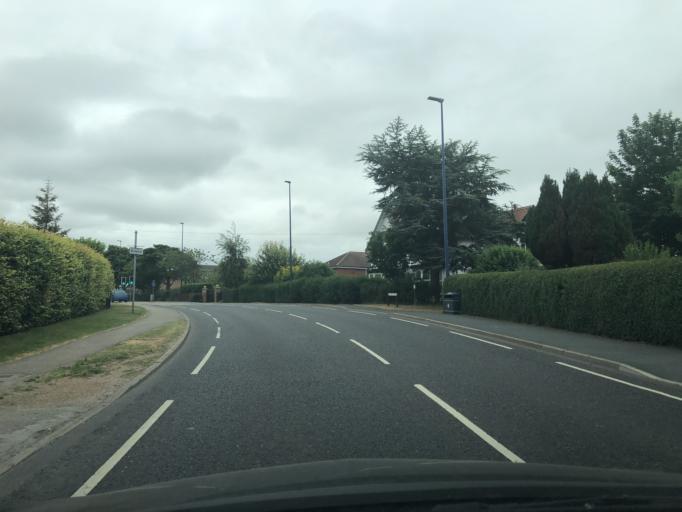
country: GB
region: England
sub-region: North Yorkshire
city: Filey
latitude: 54.2064
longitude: -0.3010
